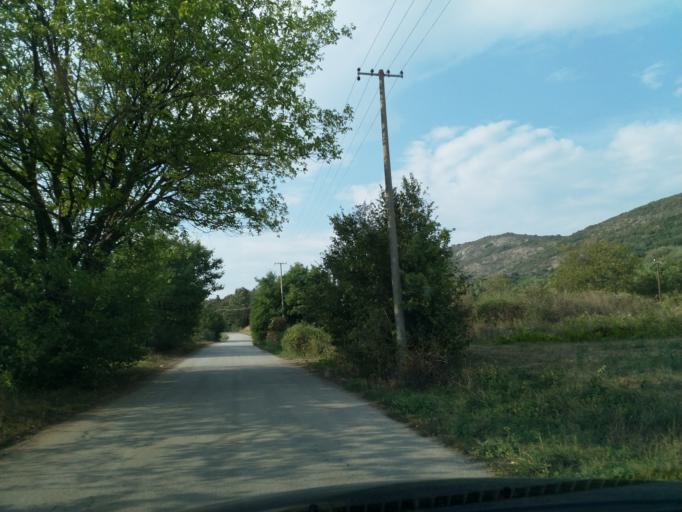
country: RS
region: Central Serbia
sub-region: Pomoravski Okrug
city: Paracin
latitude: 43.8318
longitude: 21.5418
